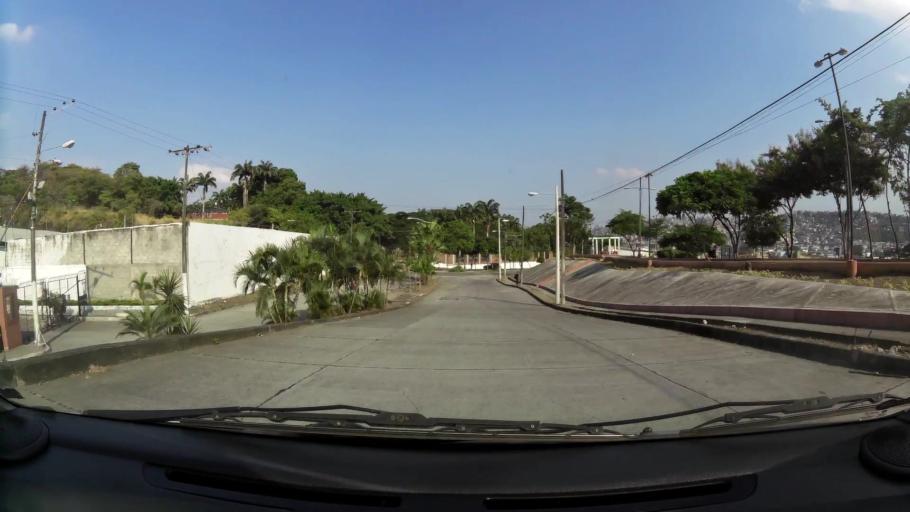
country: EC
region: Guayas
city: Guayaquil
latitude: -2.1364
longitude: -79.9248
